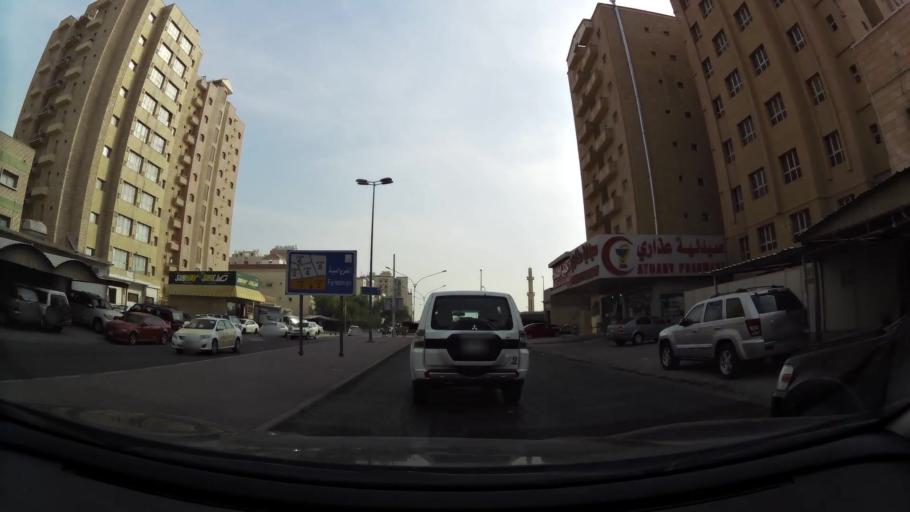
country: KW
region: Al Farwaniyah
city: Al Farwaniyah
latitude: 29.2881
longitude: 47.9549
